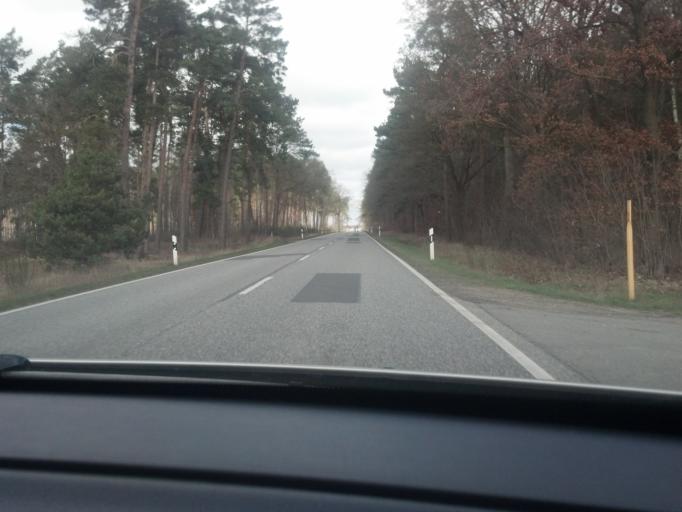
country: DE
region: Mecklenburg-Vorpommern
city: Plau am See
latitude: 53.3623
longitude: 12.2471
